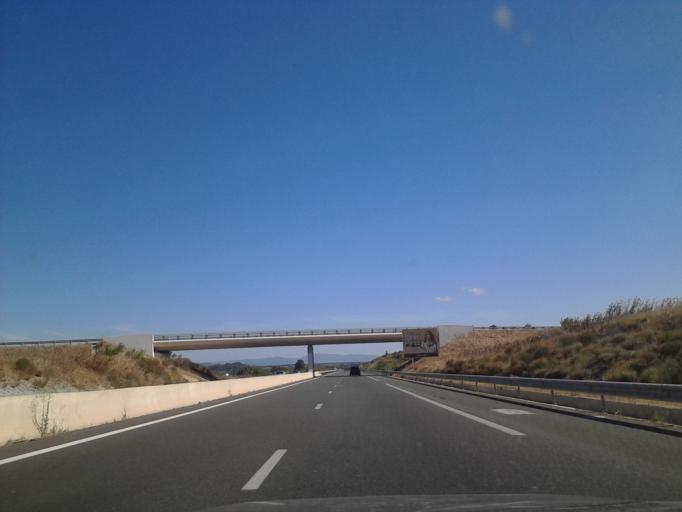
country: FR
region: Languedoc-Roussillon
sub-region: Departement de l'Herault
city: Tourbes
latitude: 43.4269
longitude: 3.3898
